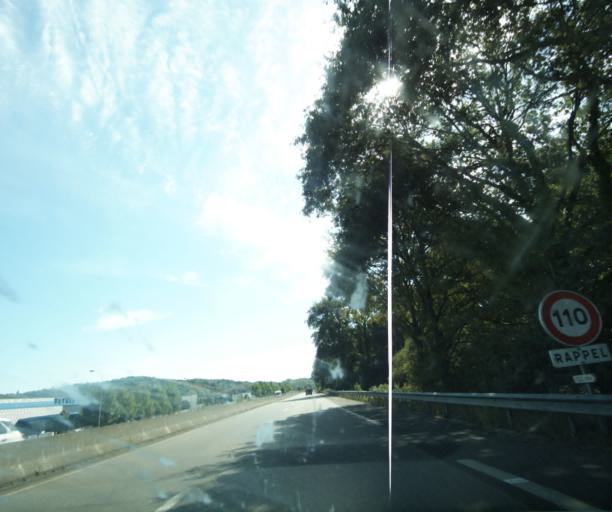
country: FR
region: Limousin
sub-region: Departement de la Correze
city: Ussac
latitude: 45.1827
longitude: 1.4915
